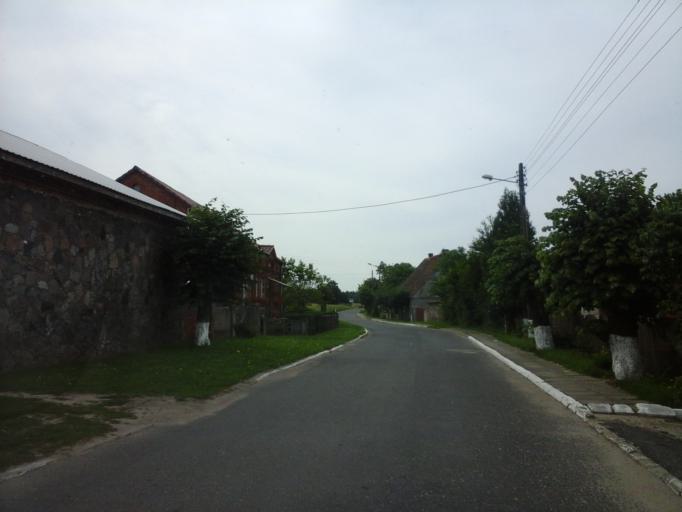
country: PL
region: West Pomeranian Voivodeship
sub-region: Powiat choszczenski
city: Recz
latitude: 53.2125
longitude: 15.5469
